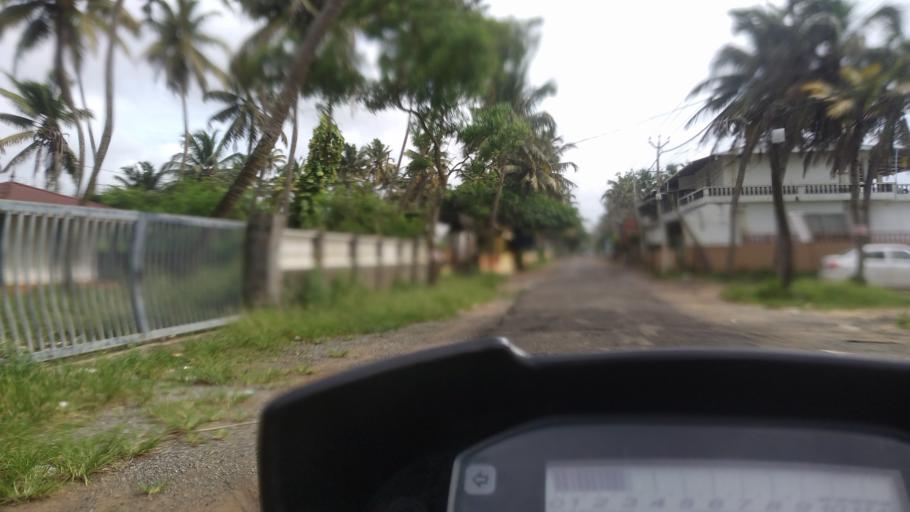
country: IN
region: Kerala
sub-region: Thrissur District
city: Kodungallur
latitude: 10.1435
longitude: 76.1780
